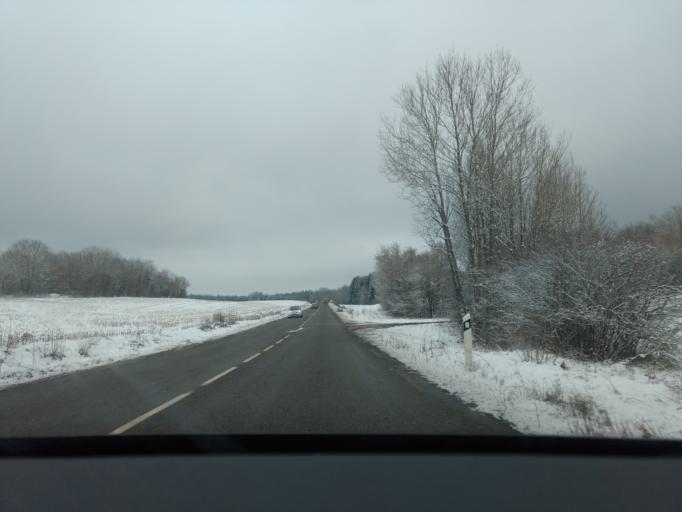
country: FR
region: Franche-Comte
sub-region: Departement du Jura
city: Champagnole
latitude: 46.7876
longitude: 5.8506
